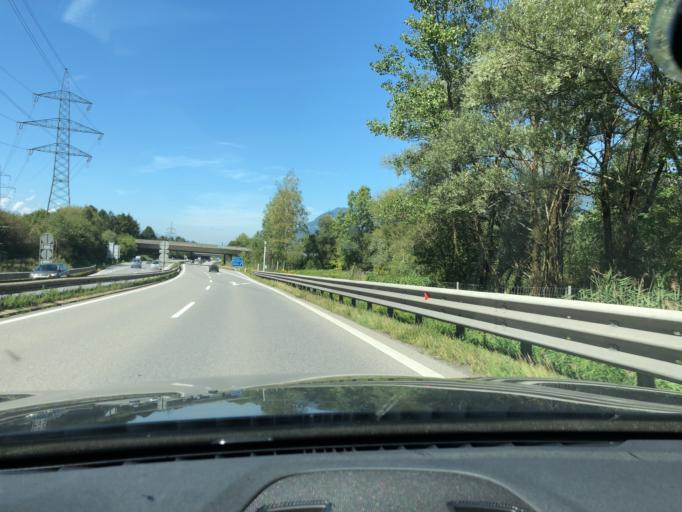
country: AT
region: Vorarlberg
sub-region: Politischer Bezirk Bludenz
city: Nuziders
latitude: 47.1640
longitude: 9.7945
